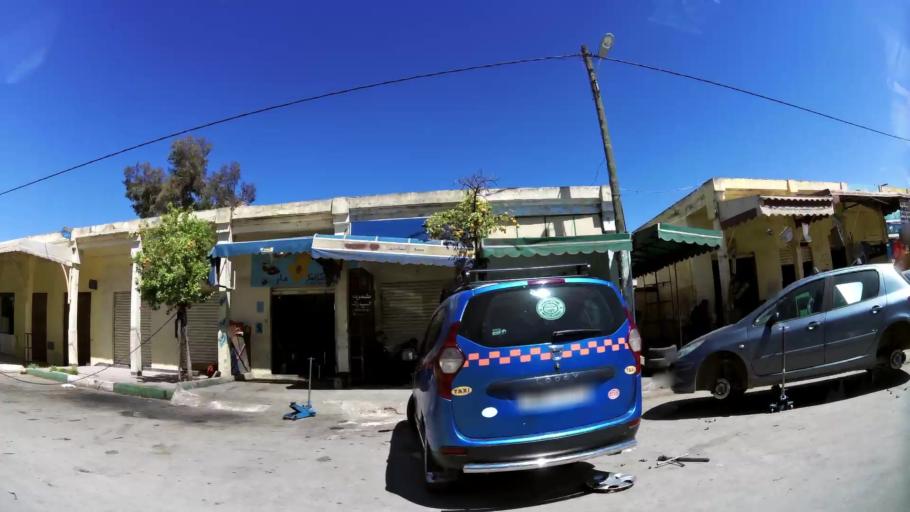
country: MA
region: Meknes-Tafilalet
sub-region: Meknes
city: Meknes
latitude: 33.8947
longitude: -5.5762
